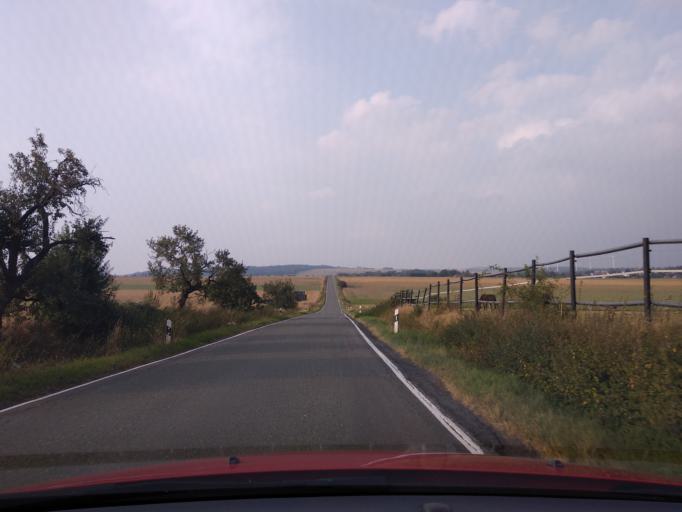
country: DE
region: North Rhine-Westphalia
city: Borgentreich
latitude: 51.5612
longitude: 9.2993
